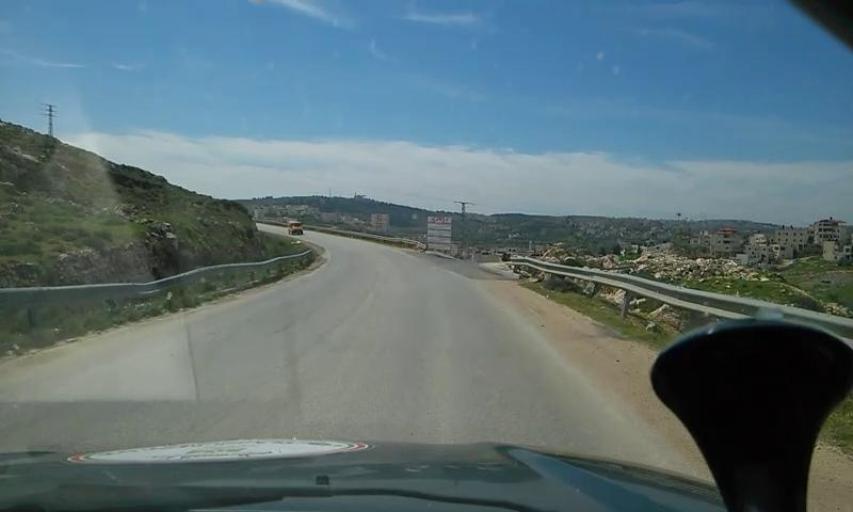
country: PS
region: West Bank
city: Al Judayrah
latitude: 31.8590
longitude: 35.2024
